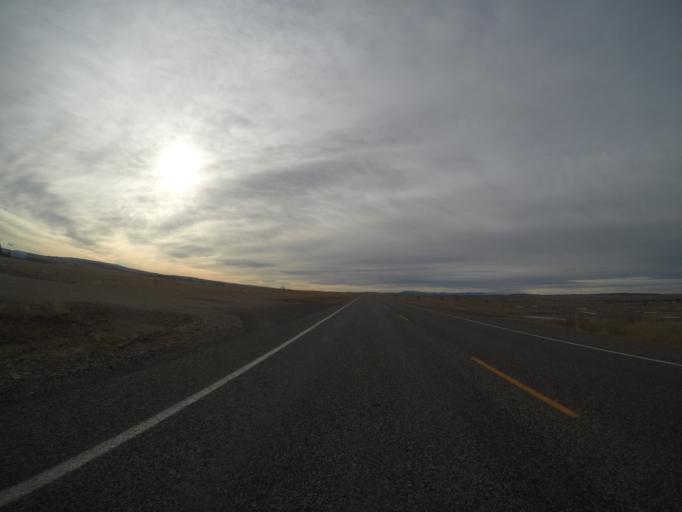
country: US
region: Montana
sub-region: Yellowstone County
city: Laurel
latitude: 45.5816
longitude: -108.8417
